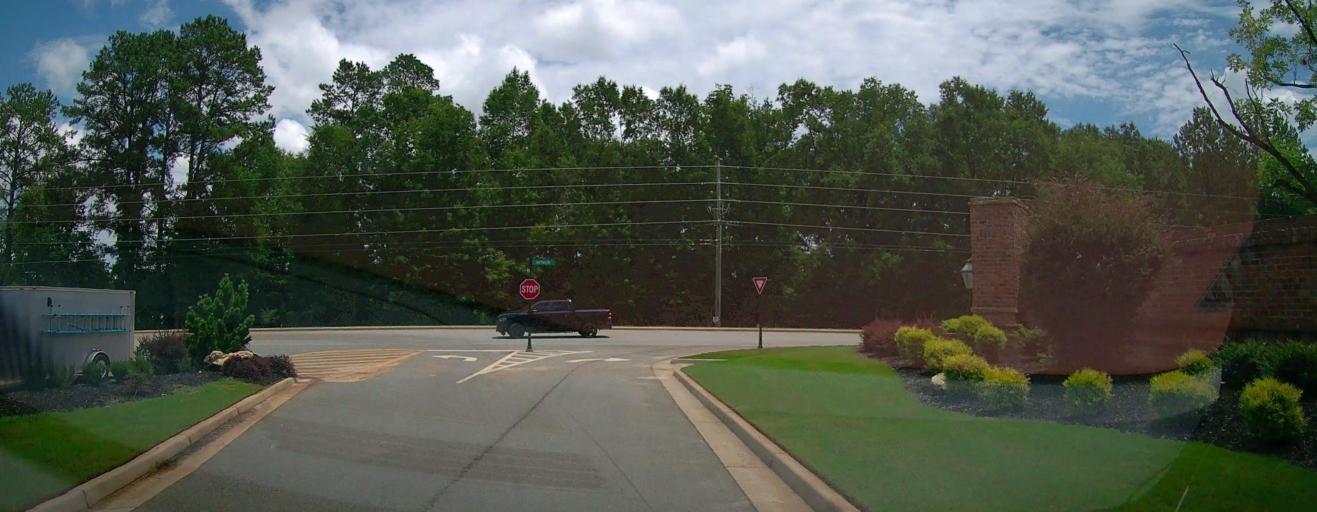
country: US
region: Georgia
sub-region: Houston County
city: Robins Air Force Base
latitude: 32.5182
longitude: -83.6142
